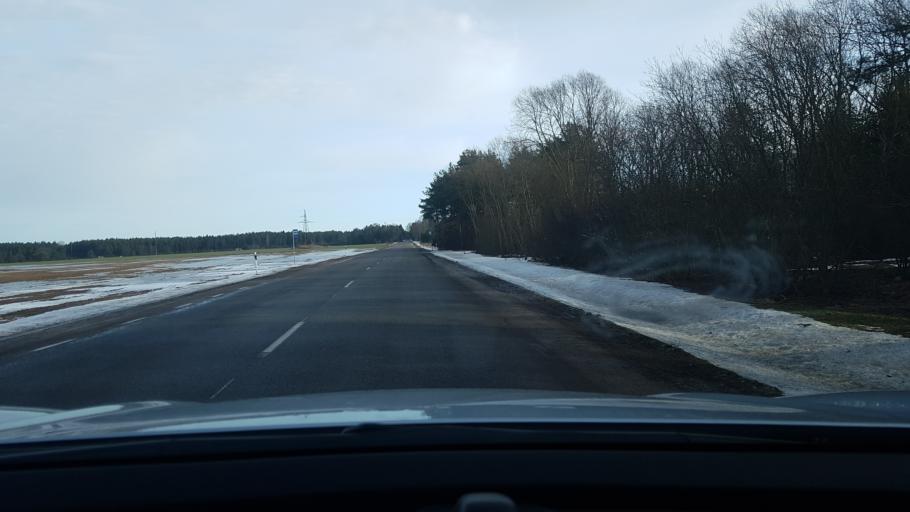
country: EE
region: Saare
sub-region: Kuressaare linn
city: Kuressaare
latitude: 58.3798
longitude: 22.6284
